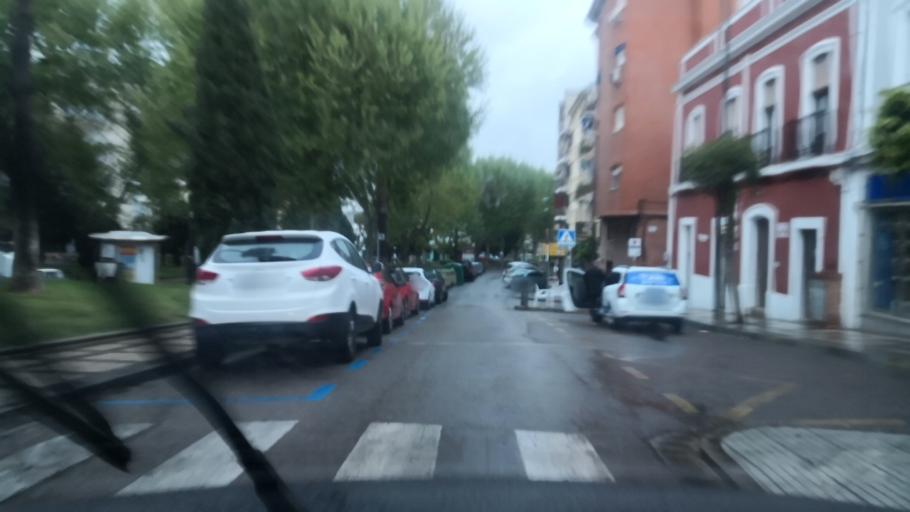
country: ES
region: Extremadura
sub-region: Provincia de Badajoz
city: Merida
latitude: 38.9184
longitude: -6.3423
